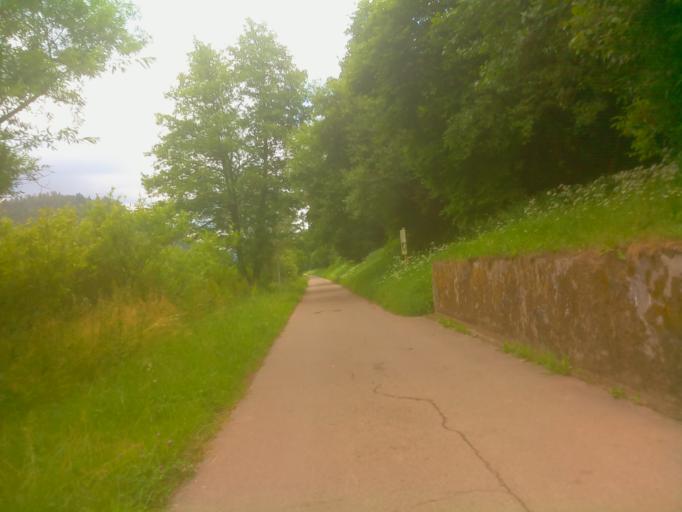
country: DE
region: Baden-Wuerttemberg
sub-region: Karlsruhe Region
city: Eberbach
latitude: 49.4561
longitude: 8.9564
